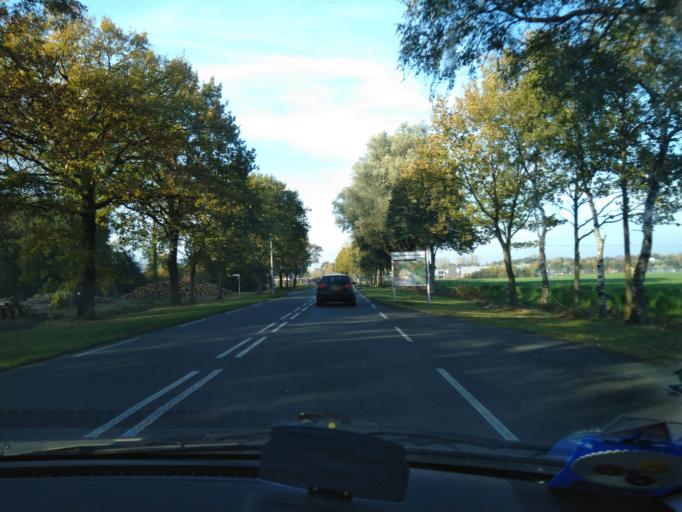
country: NL
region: Groningen
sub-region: Gemeente Hoogezand-Sappemeer
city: Hoogezand
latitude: 53.1460
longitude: 6.7654
